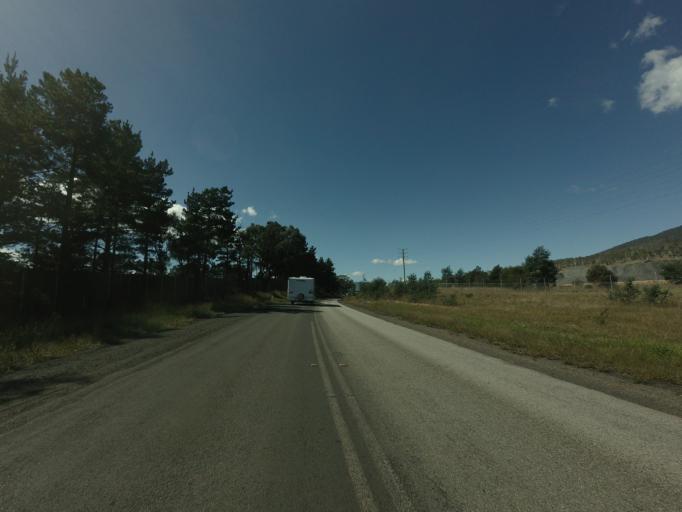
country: AU
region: Tasmania
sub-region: Break O'Day
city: St Helens
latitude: -41.6303
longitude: 147.9864
